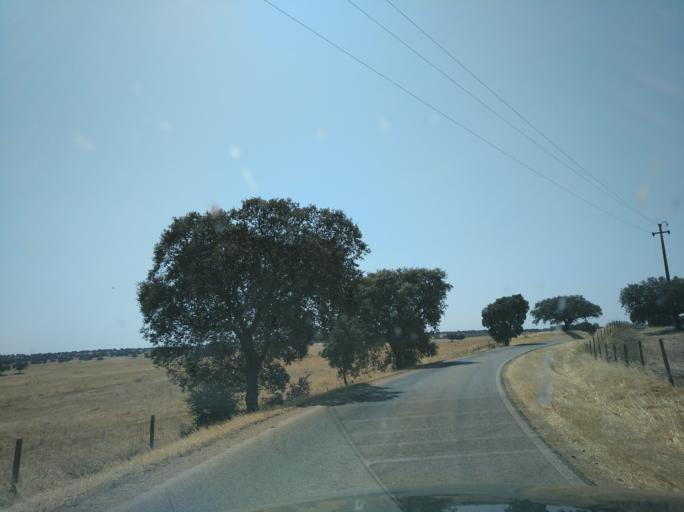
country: PT
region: Portalegre
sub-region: Campo Maior
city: Campo Maior
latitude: 39.0161
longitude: -6.9829
